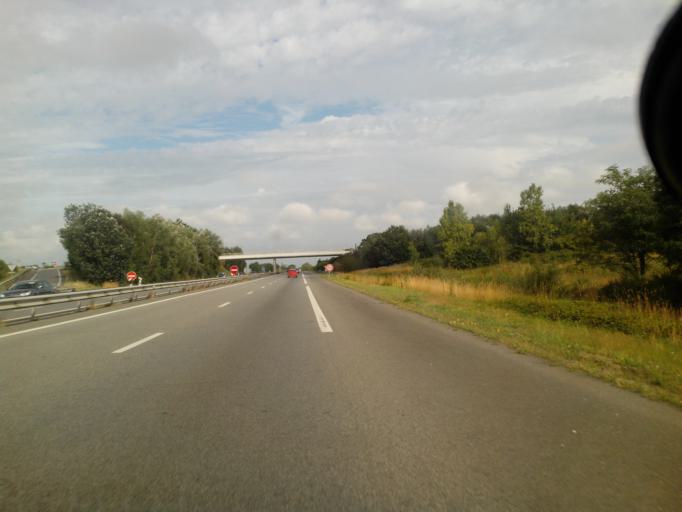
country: FR
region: Pays de la Loire
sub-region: Departement de la Loire-Atlantique
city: La Chapelle-Launay
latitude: 47.3922
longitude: -1.9937
